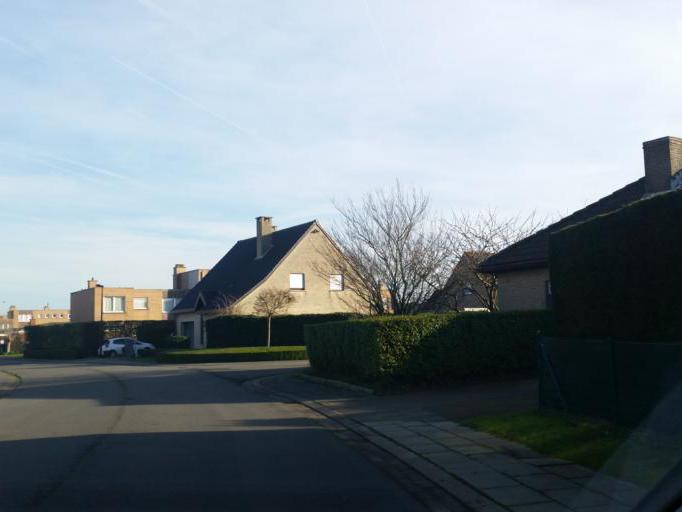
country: BE
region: Flanders
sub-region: Provincie West-Vlaanderen
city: De Haan
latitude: 51.2588
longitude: 3.0242
